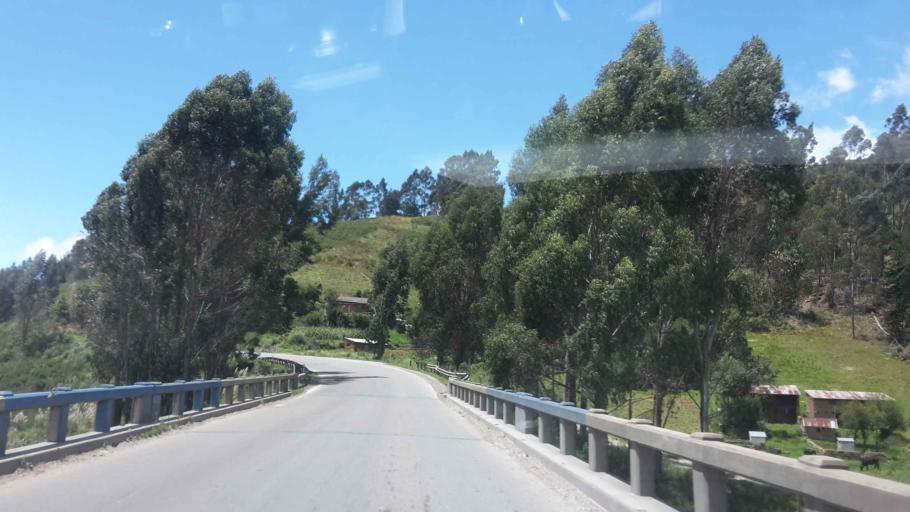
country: BO
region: Cochabamba
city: Colomi
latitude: -17.3218
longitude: -65.8736
